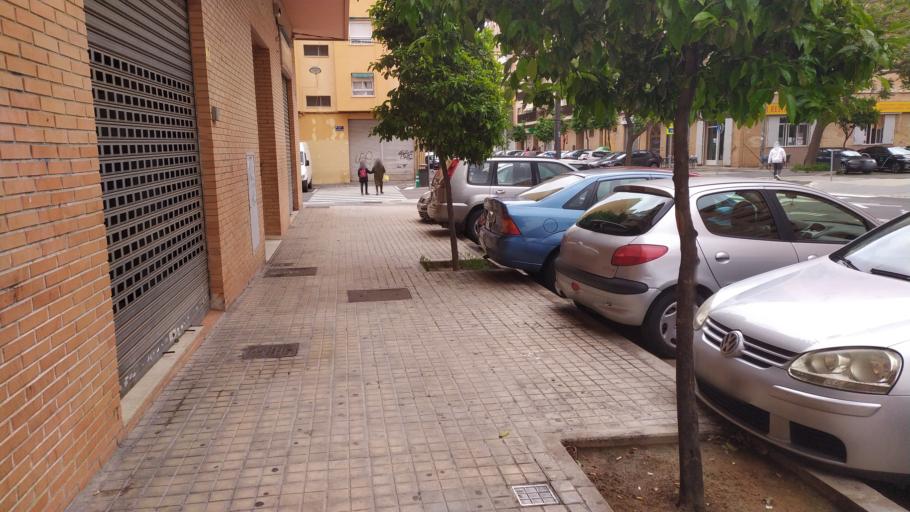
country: ES
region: Valencia
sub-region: Provincia de Valencia
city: Mislata
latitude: 39.4671
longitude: -0.4117
